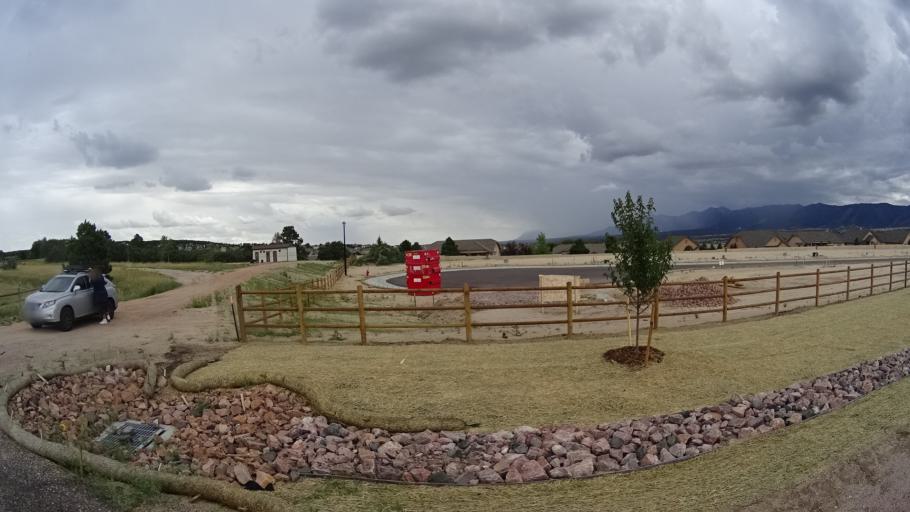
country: US
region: Colorado
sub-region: El Paso County
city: Woodmoor
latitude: 39.0977
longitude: -104.8532
